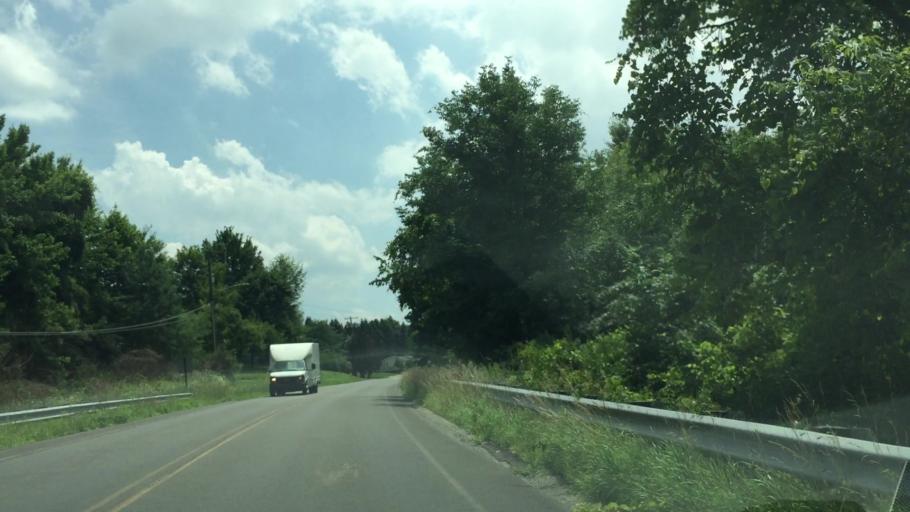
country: US
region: Pennsylvania
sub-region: Allegheny County
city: Enlow
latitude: 40.4495
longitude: -80.2329
